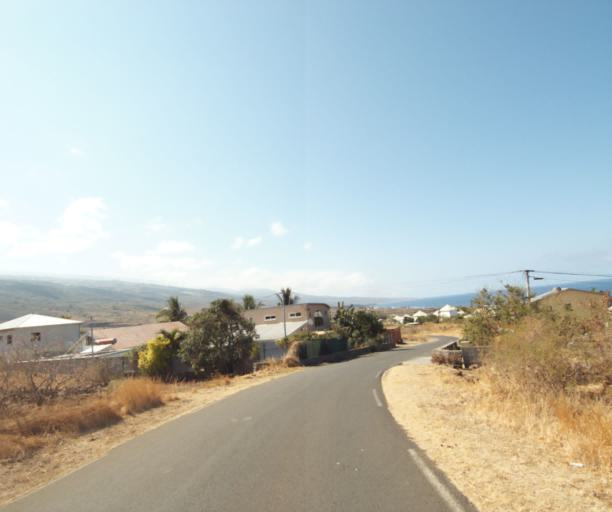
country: RE
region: Reunion
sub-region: Reunion
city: Trois-Bassins
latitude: -21.1028
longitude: 55.2515
